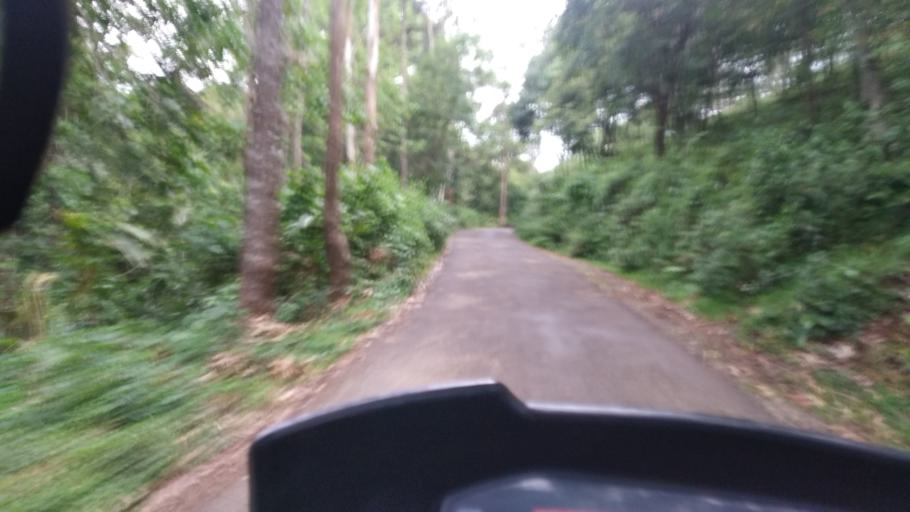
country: IN
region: Tamil Nadu
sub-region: Theni
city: Gudalur
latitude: 9.5490
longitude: 77.0553
